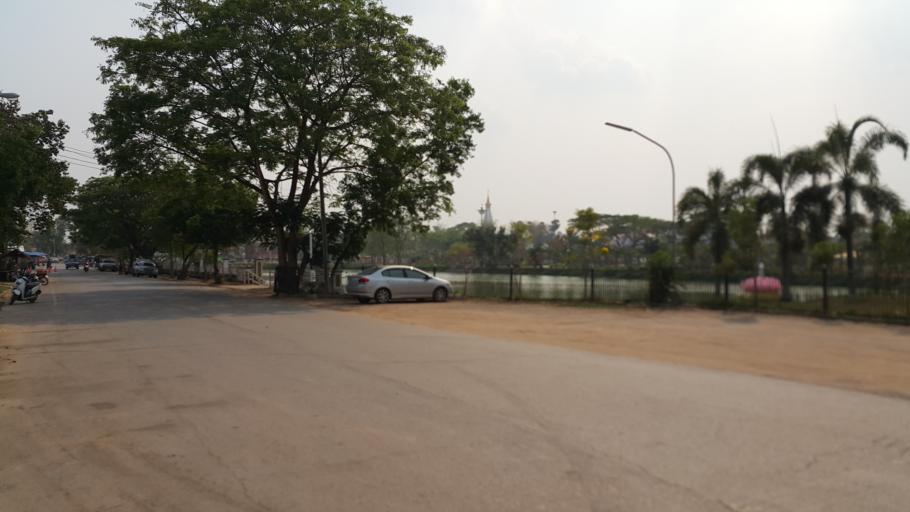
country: TH
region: Nakhon Phanom
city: That Phanom
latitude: 16.9464
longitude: 104.7278
